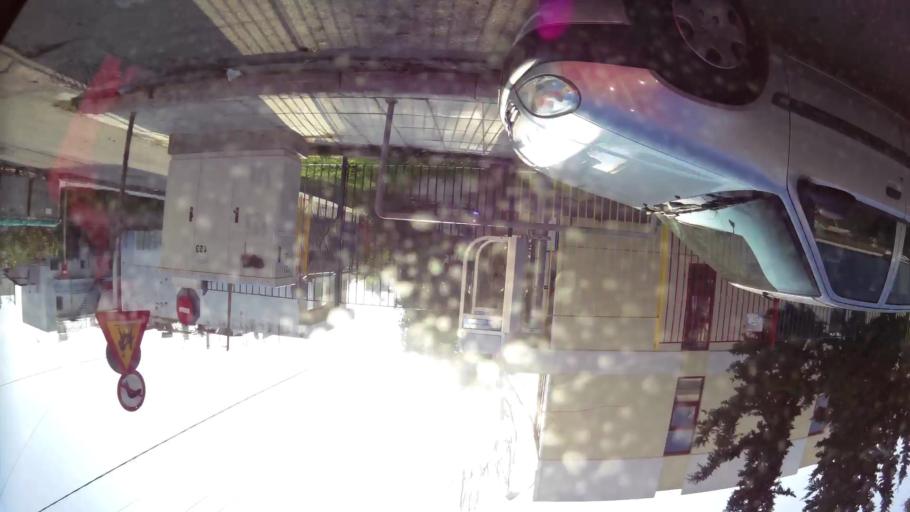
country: GR
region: Attica
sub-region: Nomarchia Athinas
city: Nea Filadelfeia
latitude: 38.0533
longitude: 23.7348
